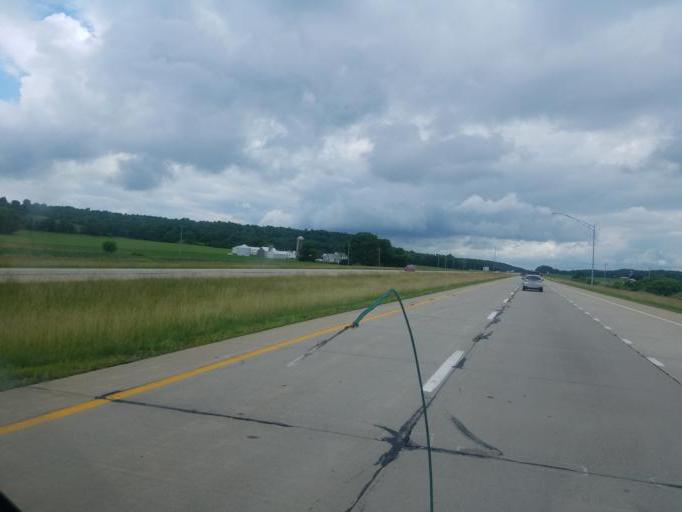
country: US
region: Ohio
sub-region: Logan County
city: Bellefontaine
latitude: 40.3244
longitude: -83.6561
